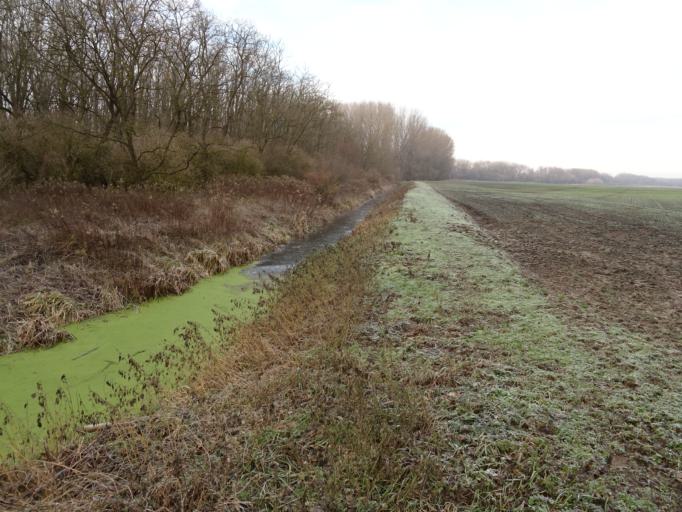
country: HU
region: Gyor-Moson-Sopron
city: Kony
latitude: 47.6108
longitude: 17.3515
